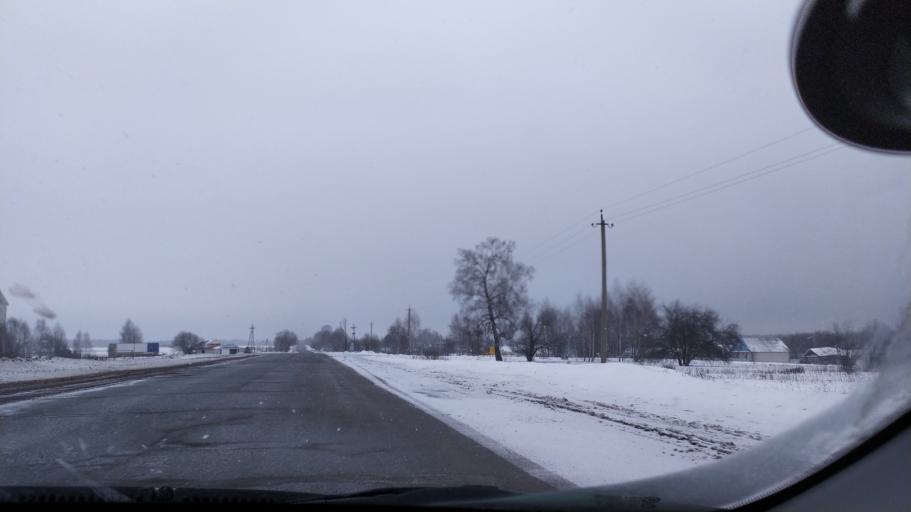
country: RU
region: Mariy-El
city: Krasnogorskiy
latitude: 56.1480
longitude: 48.1333
